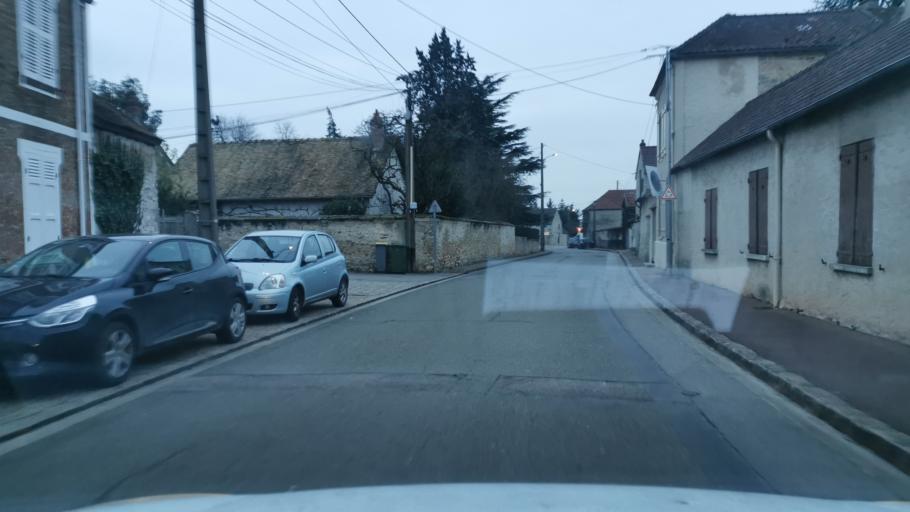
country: FR
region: Ile-de-France
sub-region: Departement des Yvelines
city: Longnes
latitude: 48.9204
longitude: 1.5878
